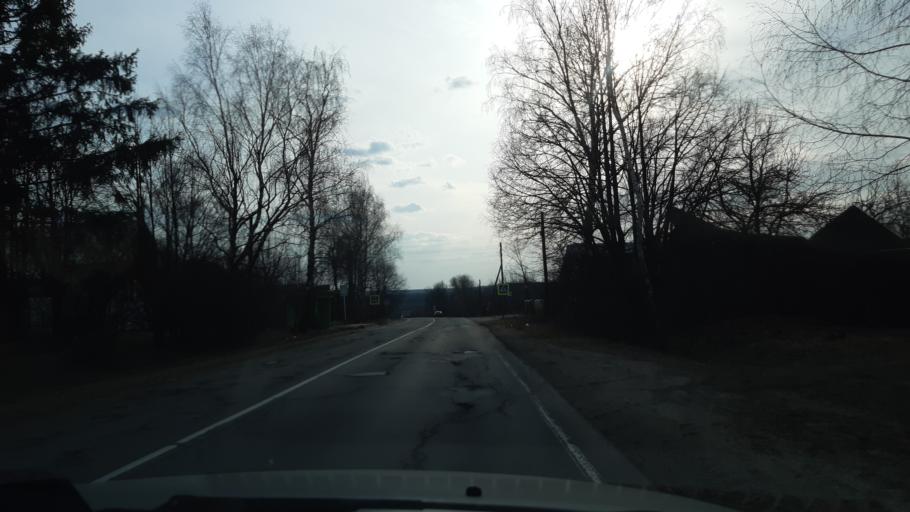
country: RU
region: Vladimir
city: Luknovo
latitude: 56.1888
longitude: 42.0225
